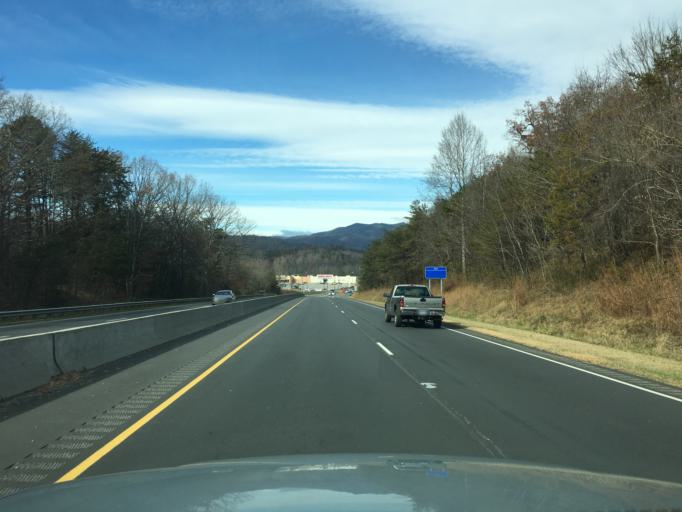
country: US
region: North Carolina
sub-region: McDowell County
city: Marion
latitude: 35.7007
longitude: -82.0331
